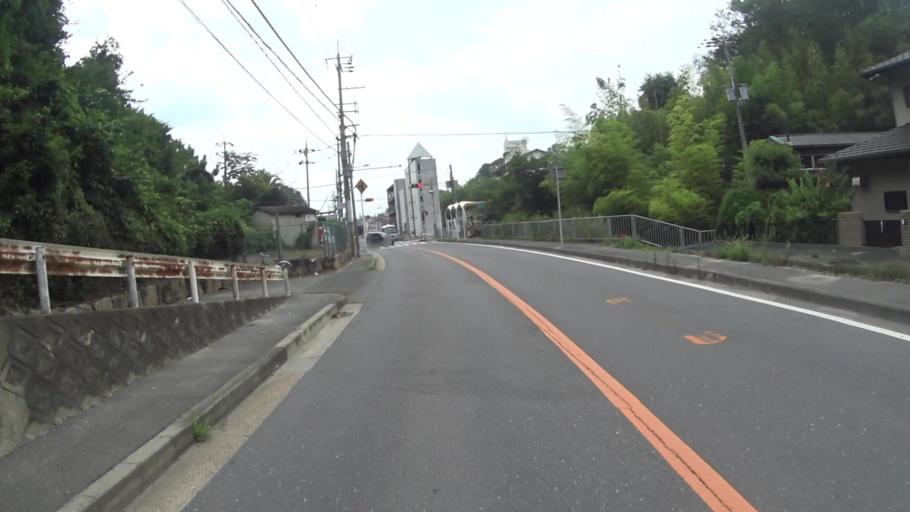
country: JP
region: Kyoto
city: Tanabe
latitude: 34.8071
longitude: 135.7244
